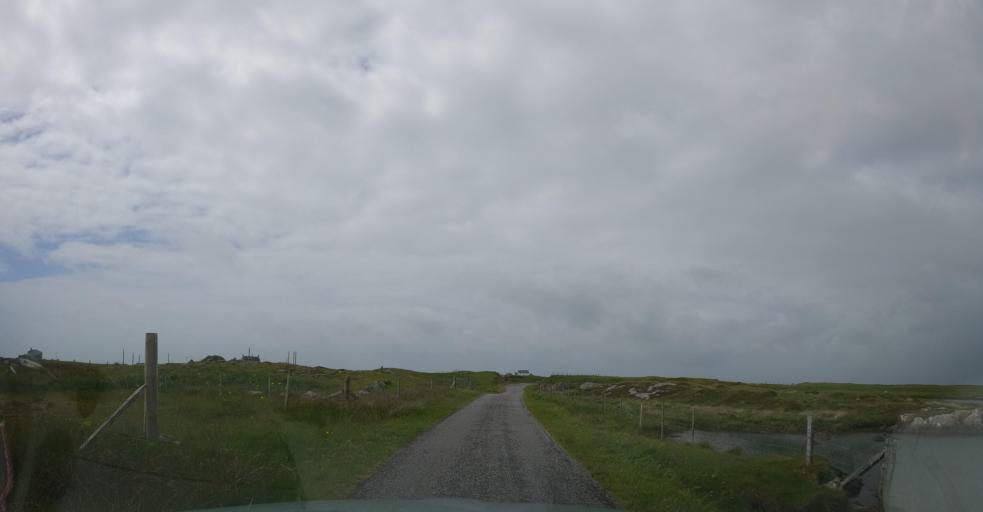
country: GB
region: Scotland
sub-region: Eilean Siar
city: Isle of South Uist
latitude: 57.2422
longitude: -7.4049
